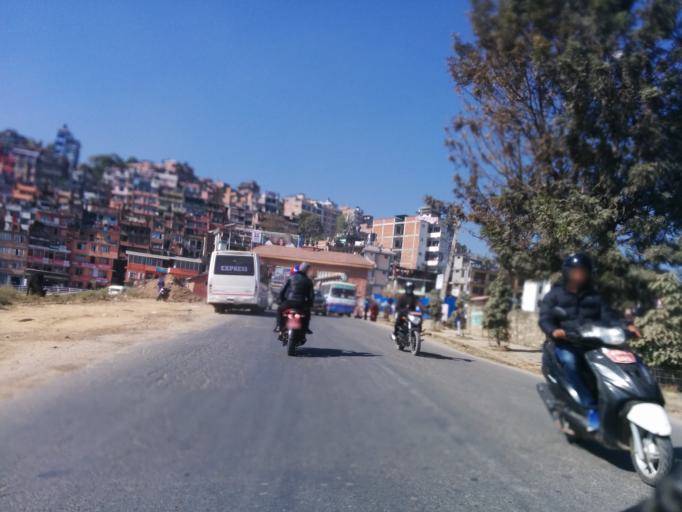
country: NP
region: Central Region
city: Kirtipur
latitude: 27.6771
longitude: 85.2825
